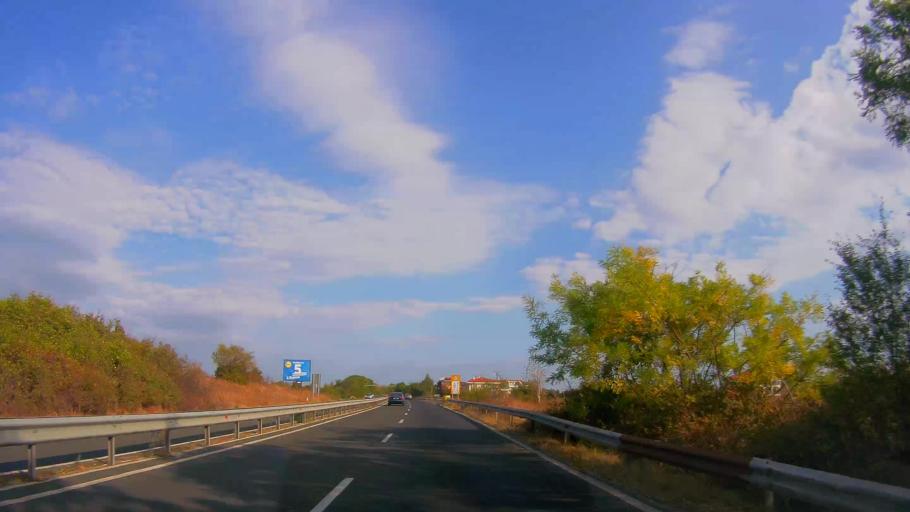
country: BG
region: Burgas
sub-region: Obshtina Sozopol
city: Chernomorets
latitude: 42.4297
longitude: 27.6397
